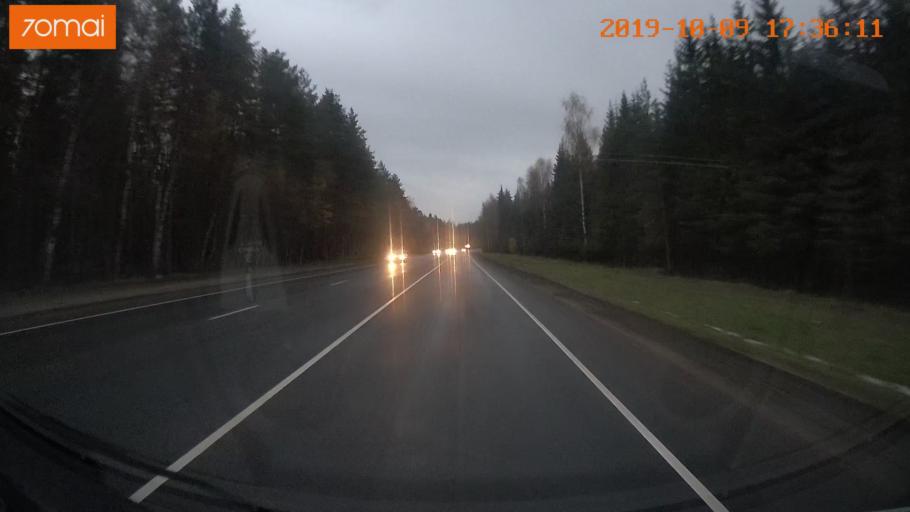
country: RU
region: Ivanovo
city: Bogorodskoye
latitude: 57.0821
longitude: 40.9982
